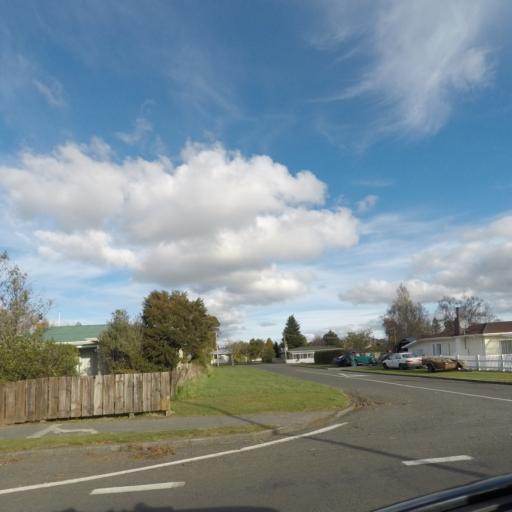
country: NZ
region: Manawatu-Wanganui
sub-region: Ruapehu District
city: Waiouru
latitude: -39.4089
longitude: 175.4078
